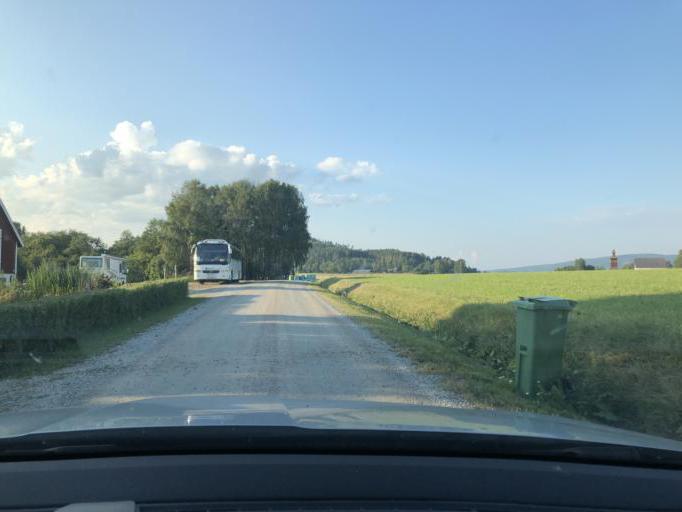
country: SE
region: Vaesternorrland
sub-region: Kramfors Kommun
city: Bollstabruk
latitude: 63.0755
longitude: 17.7364
